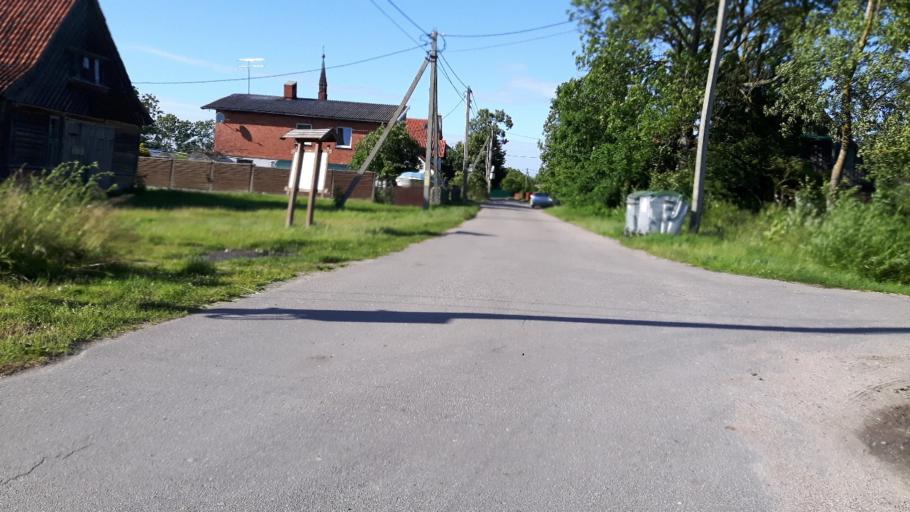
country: LT
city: Nida
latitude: 55.1520
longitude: 20.8549
